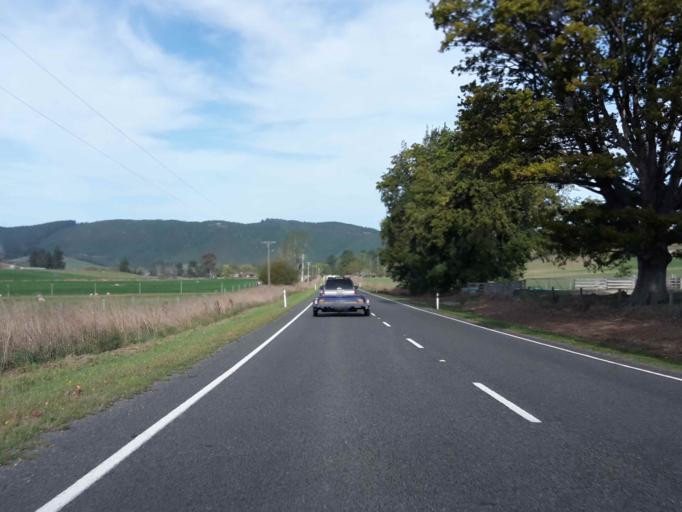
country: NZ
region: Canterbury
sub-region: Timaru District
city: Pleasant Point
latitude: -44.1143
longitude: 171.0179
